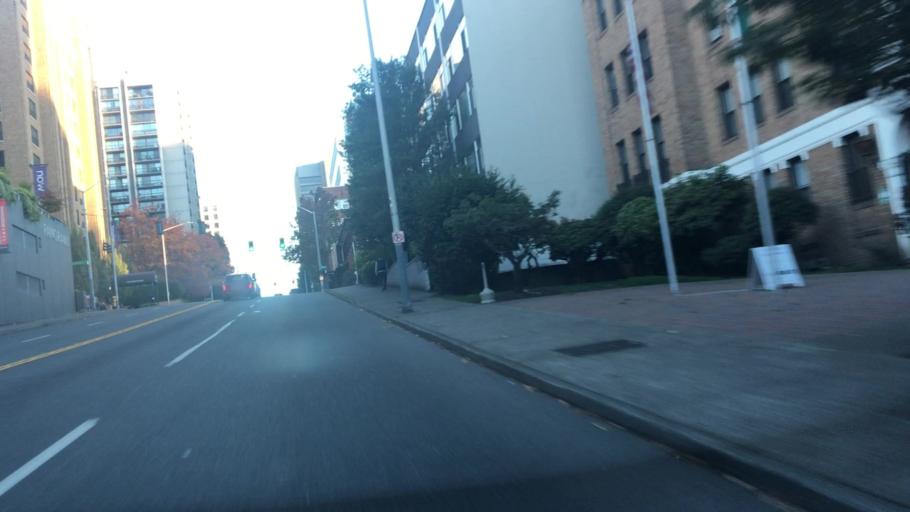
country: US
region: Washington
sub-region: King County
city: Seattle
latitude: 47.6121
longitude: -122.3277
